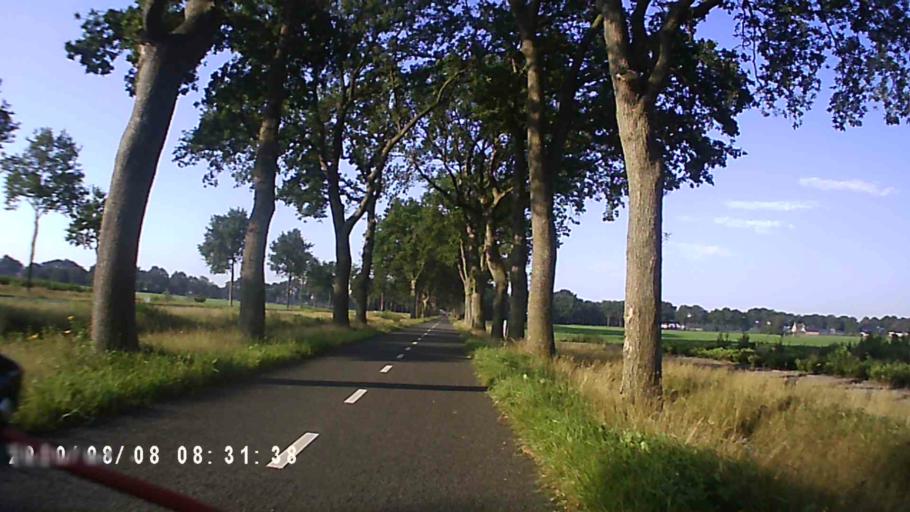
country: NL
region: Groningen
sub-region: Gemeente Leek
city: Leek
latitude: 53.0784
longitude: 6.3346
